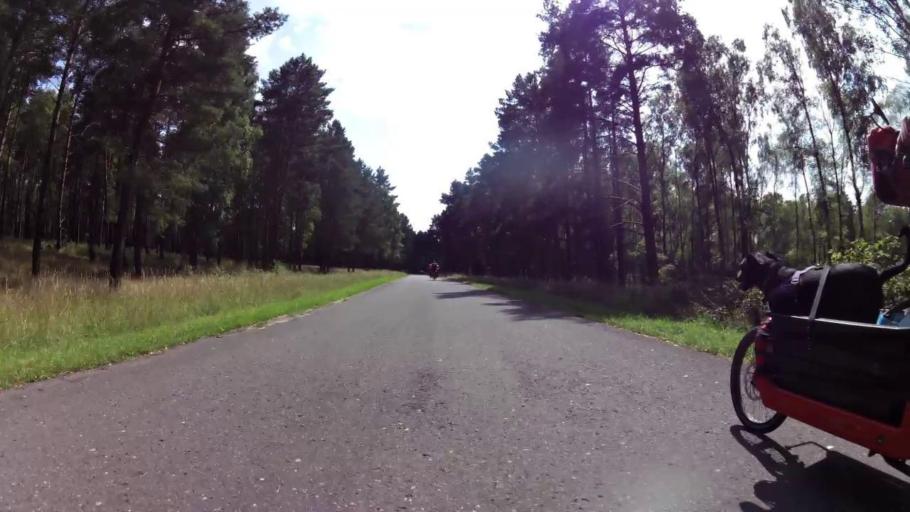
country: PL
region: West Pomeranian Voivodeship
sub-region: Powiat choszczenski
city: Drawno
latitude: 53.3542
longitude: 15.7023
